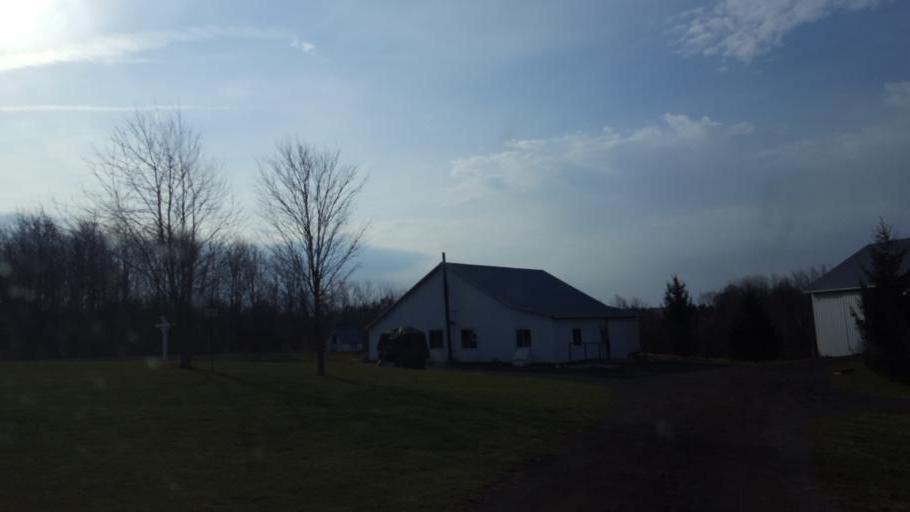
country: US
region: Ohio
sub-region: Knox County
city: Fredericktown
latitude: 40.5278
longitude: -82.6116
